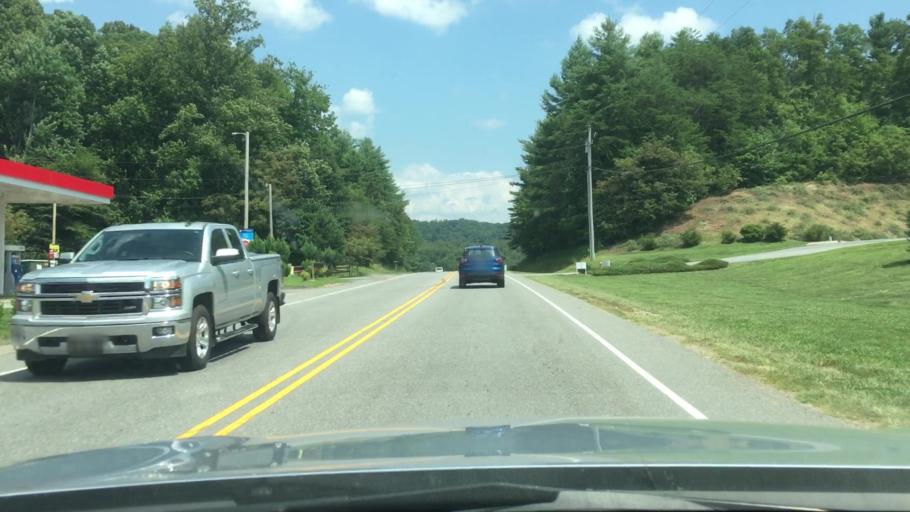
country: US
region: North Carolina
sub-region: Madison County
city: Mars Hill
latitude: 35.8259
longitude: -82.5700
